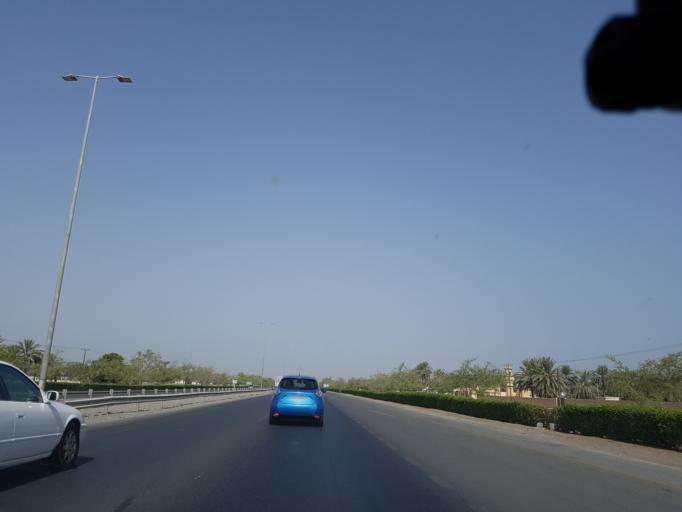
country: OM
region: Al Batinah
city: Barka'
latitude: 23.7310
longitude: 57.7004
